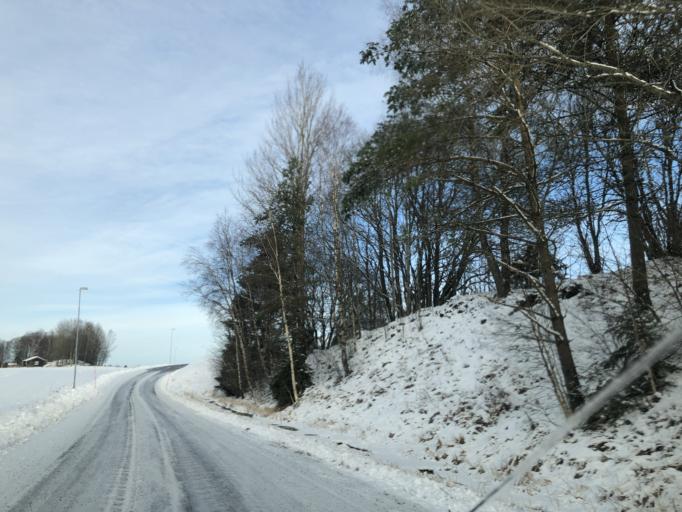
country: SE
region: Vaestra Goetaland
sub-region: Ulricehamns Kommun
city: Ulricehamn
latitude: 57.7921
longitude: 13.5328
